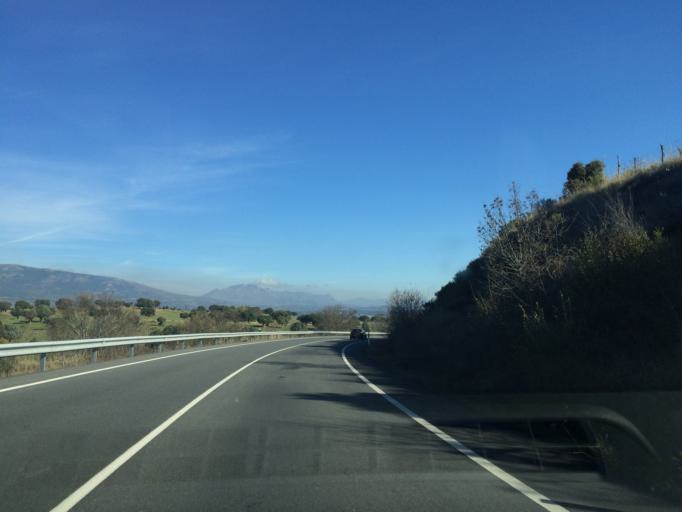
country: ES
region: Madrid
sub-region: Provincia de Madrid
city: Guadalix de la Sierra
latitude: 40.7799
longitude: -3.7233
